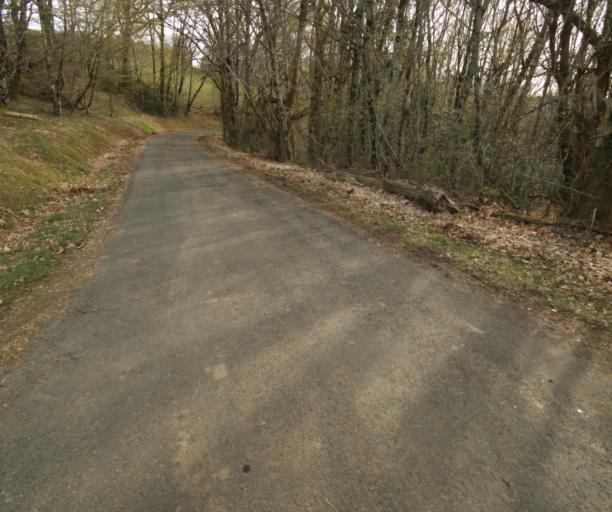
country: FR
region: Limousin
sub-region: Departement de la Correze
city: Seilhac
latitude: 45.4104
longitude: 1.7842
